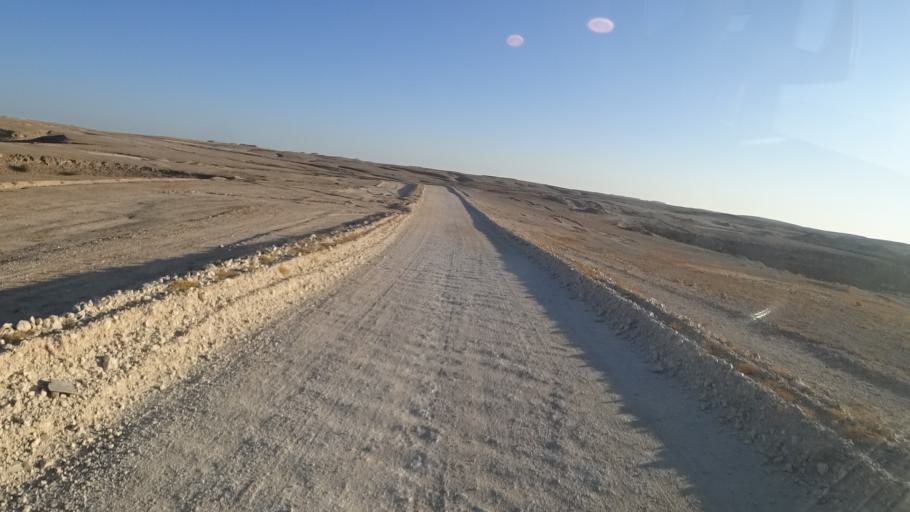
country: YE
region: Al Mahrah
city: Hawf
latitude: 17.1786
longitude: 53.3438
